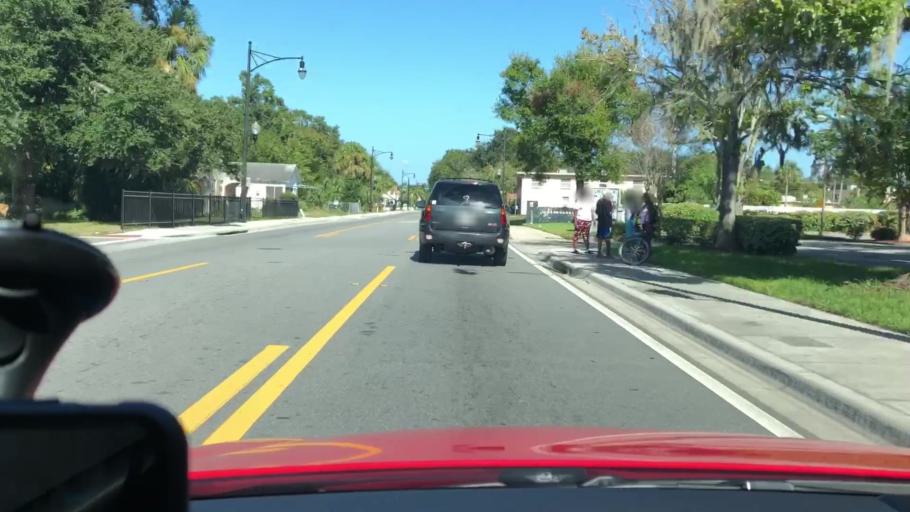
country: US
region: Florida
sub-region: Volusia County
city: Daytona Beach
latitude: 29.2039
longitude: -81.0284
